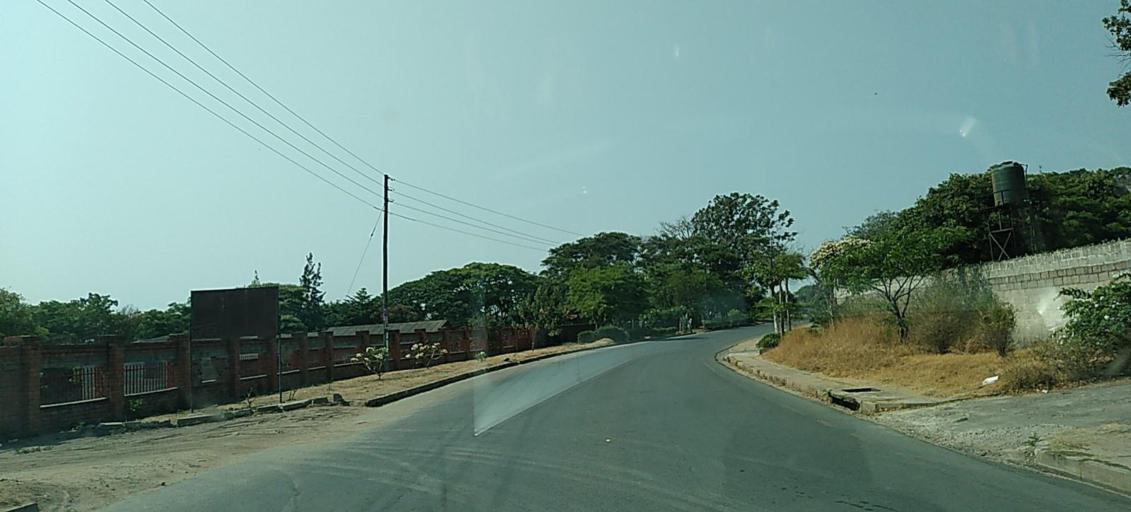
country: ZM
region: Copperbelt
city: Chingola
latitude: -12.5448
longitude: 27.8710
